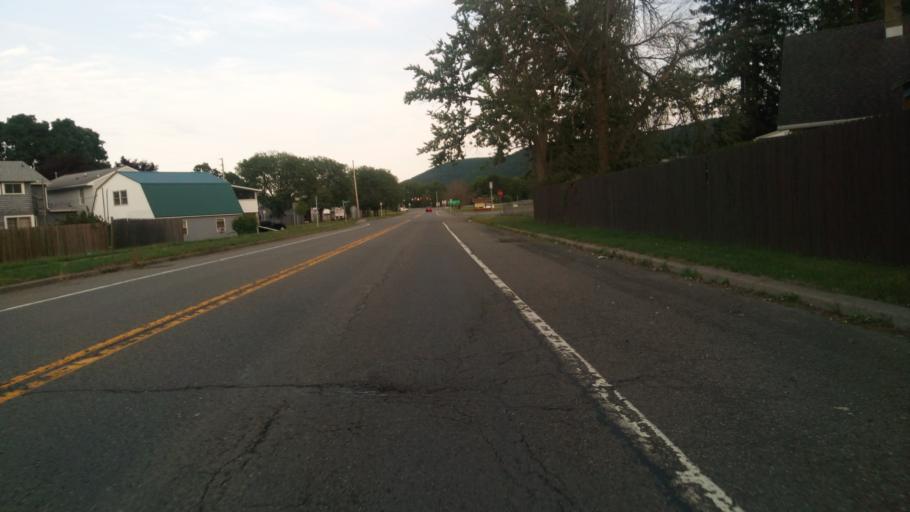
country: US
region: New York
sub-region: Chemung County
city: Southport
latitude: 42.0600
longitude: -76.8099
